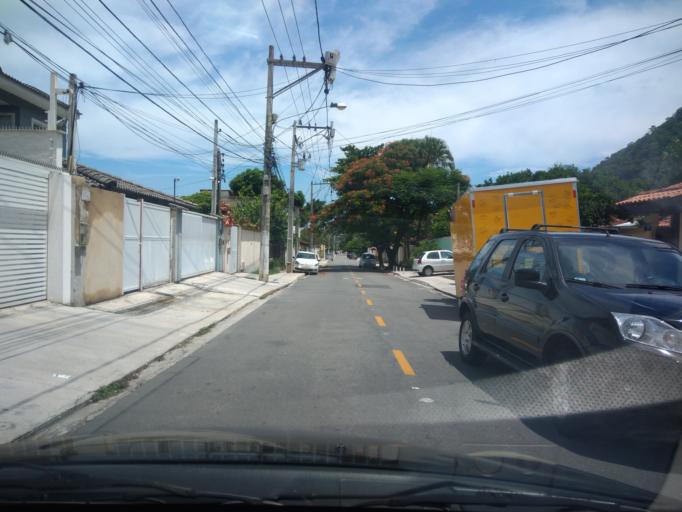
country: BR
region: Rio de Janeiro
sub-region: Niteroi
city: Niteroi
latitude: -22.9296
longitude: -43.0715
